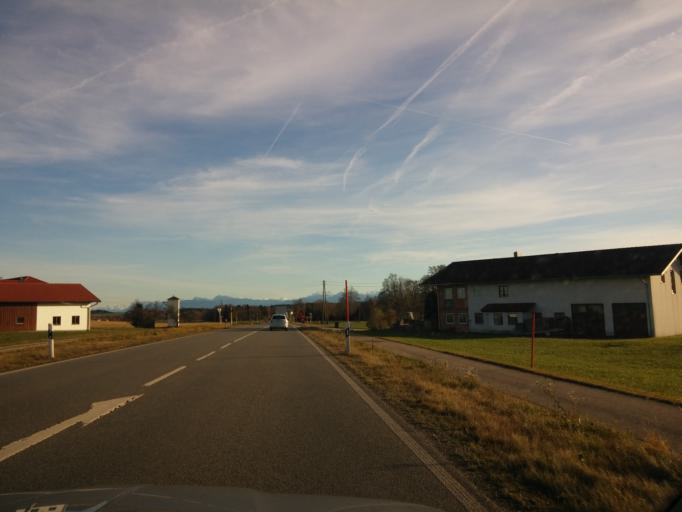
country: DE
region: Bavaria
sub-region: Upper Bavaria
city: Obing
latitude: 48.0136
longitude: 12.3880
